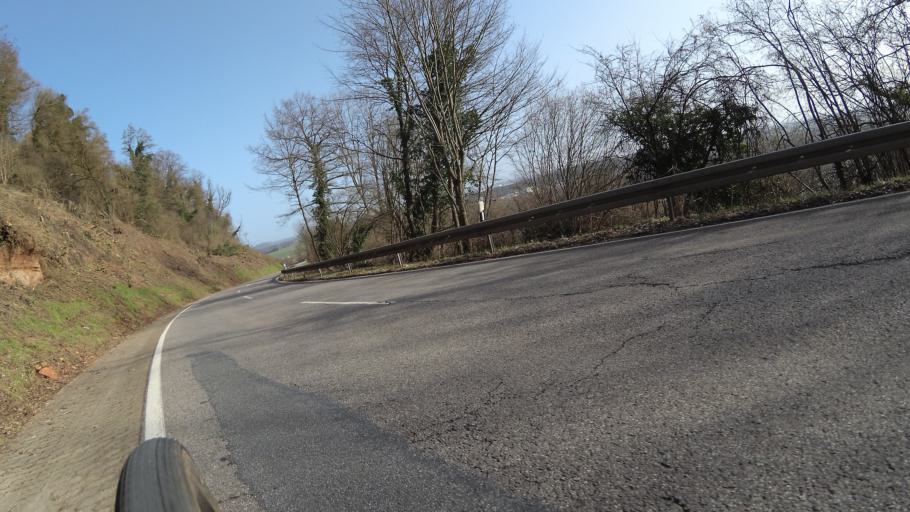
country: DE
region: Saarland
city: Uberherrn
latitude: 49.2642
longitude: 6.6995
